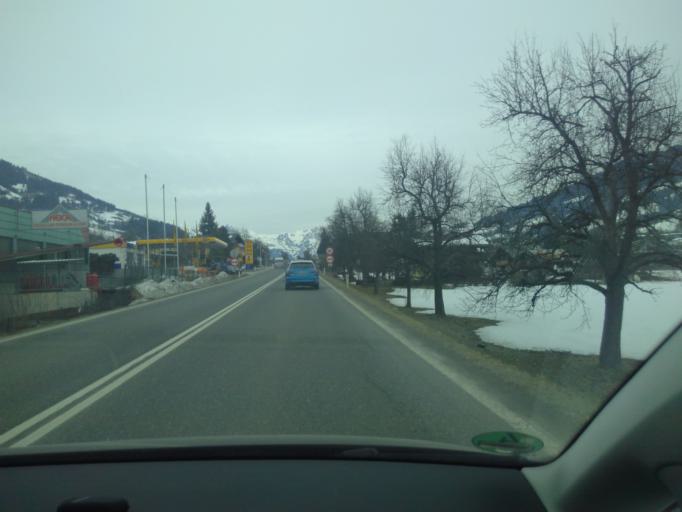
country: AT
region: Salzburg
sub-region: Politischer Bezirk Sankt Johann im Pongau
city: Sankt Johann im Pongau
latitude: 47.3427
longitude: 13.1916
